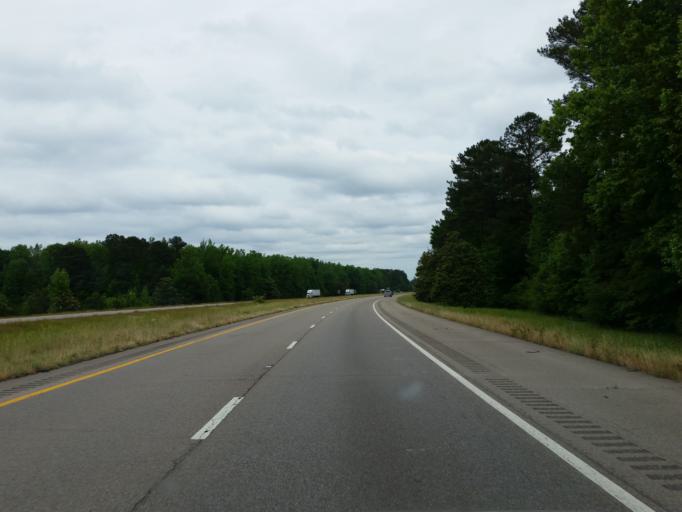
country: US
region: Mississippi
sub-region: Lauderdale County
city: Marion
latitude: 32.4130
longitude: -88.5220
